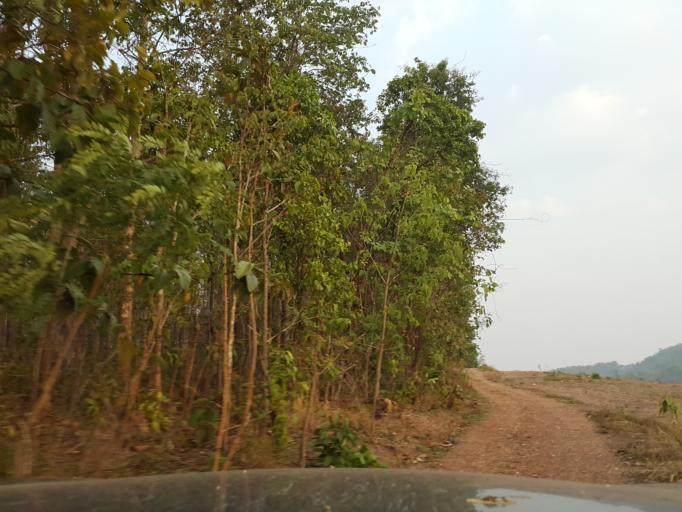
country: TH
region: Lamphun
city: Thung Hua Chang
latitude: 17.9168
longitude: 99.0727
